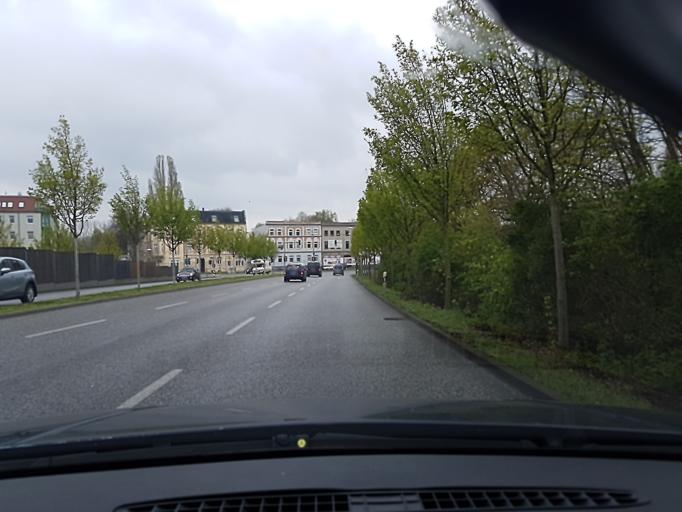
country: DE
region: Berlin
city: Adlershof
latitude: 52.4382
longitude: 13.5614
